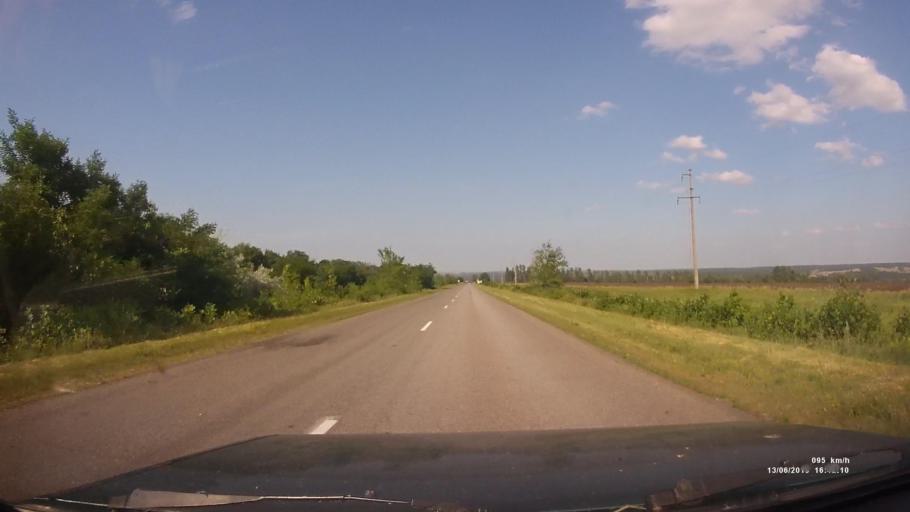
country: RU
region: Rostov
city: Kazanskaya
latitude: 49.9404
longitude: 41.3985
